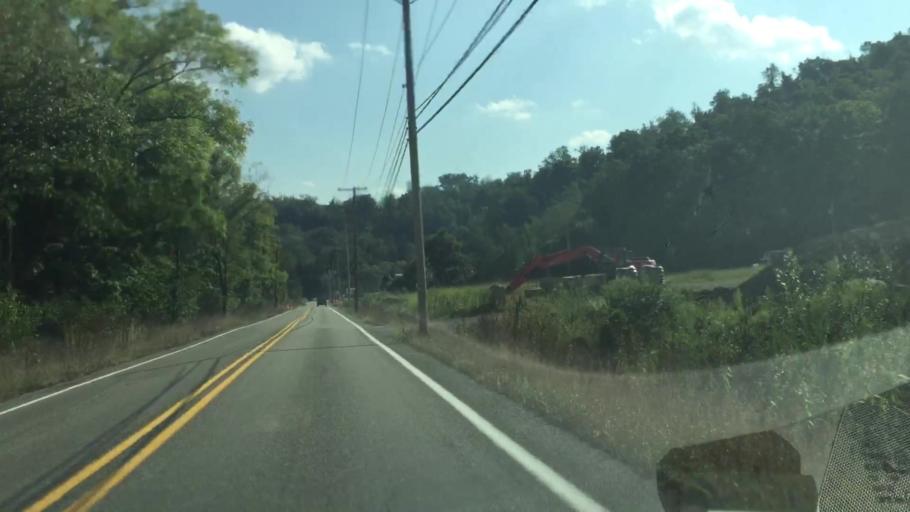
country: US
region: Pennsylvania
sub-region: Allegheny County
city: Franklin Park
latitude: 40.5547
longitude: -80.0869
